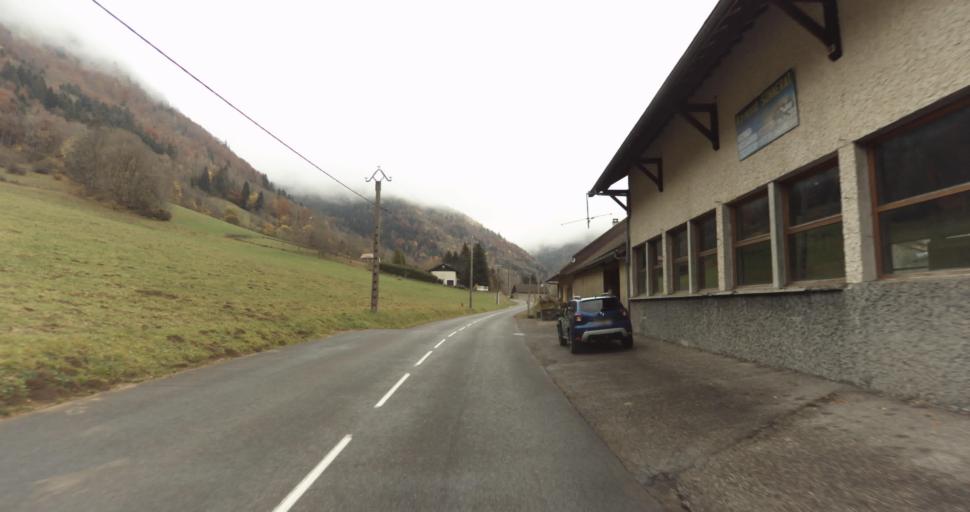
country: FR
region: Rhone-Alpes
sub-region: Departement de la Haute-Savoie
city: Thorens-Glieres
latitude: 45.9766
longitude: 6.2868
